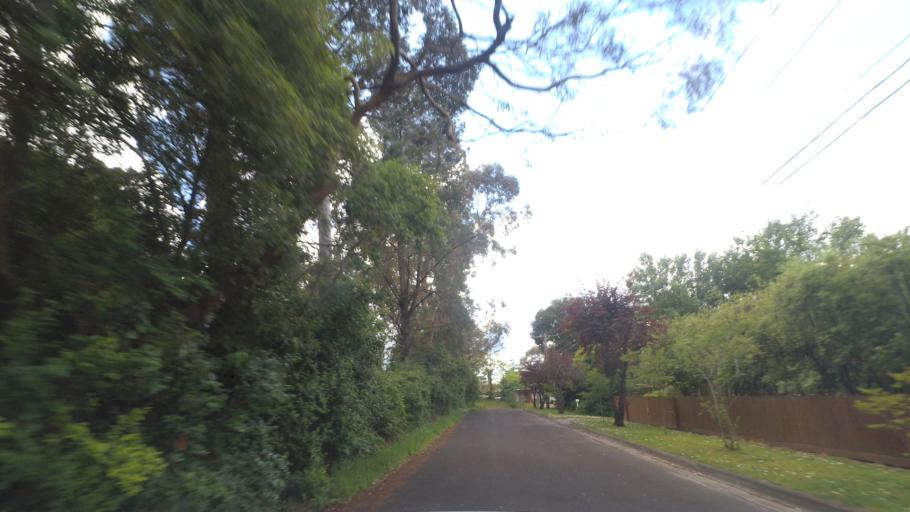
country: AU
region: Victoria
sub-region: Maroondah
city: Croydon South
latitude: -37.8043
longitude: 145.2708
